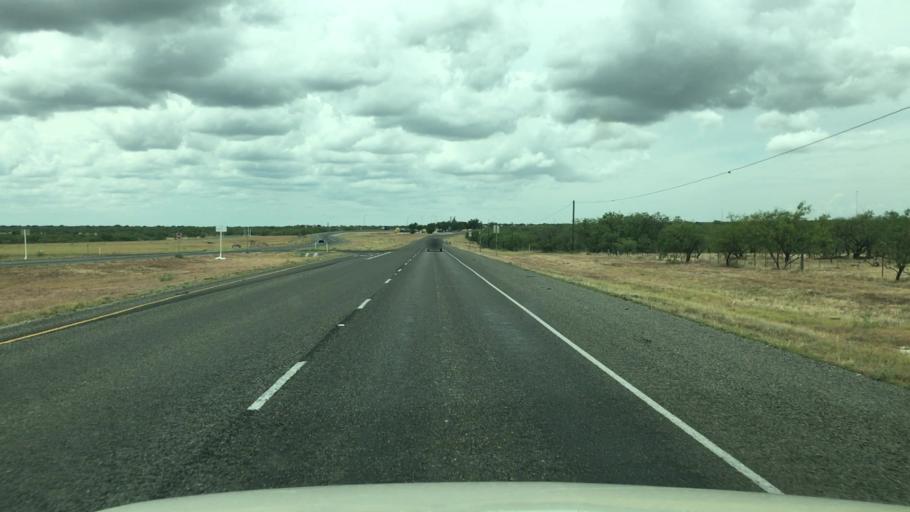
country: US
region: Texas
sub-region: Concho County
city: Eden
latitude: 31.2175
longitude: -99.9533
